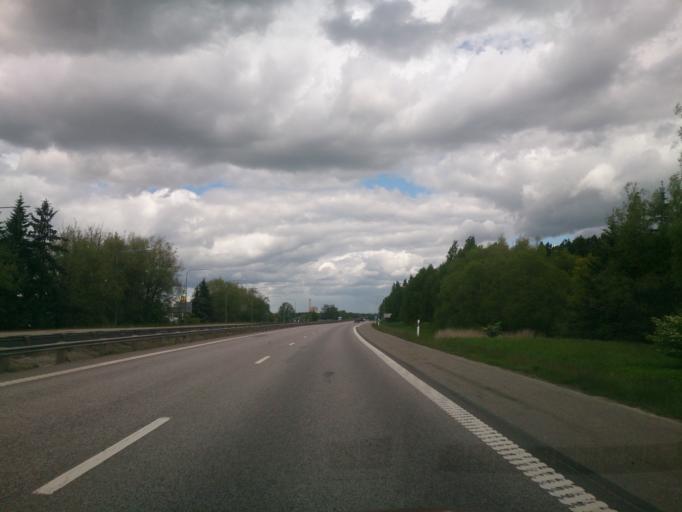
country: SE
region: OEstergoetland
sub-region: Norrkopings Kommun
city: Norrkoping
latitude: 58.5709
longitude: 16.2151
